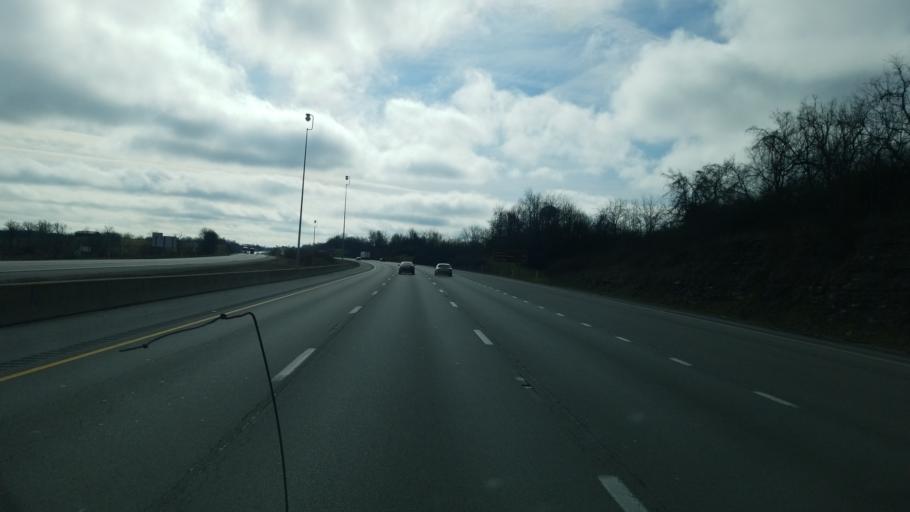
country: US
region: Kentucky
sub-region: Madison County
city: Richmond
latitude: 37.8728
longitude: -84.3341
